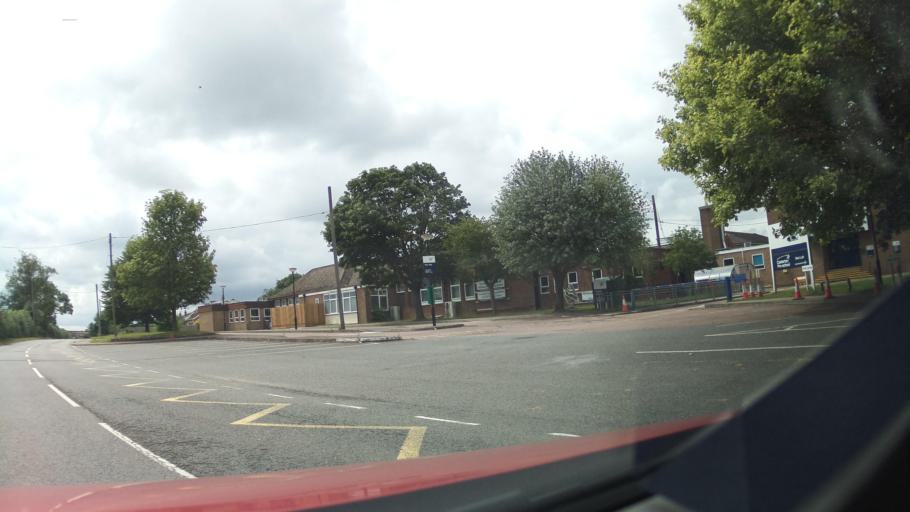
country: GB
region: England
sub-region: District of Rutland
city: Tickencote
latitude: 52.6733
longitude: -0.5167
